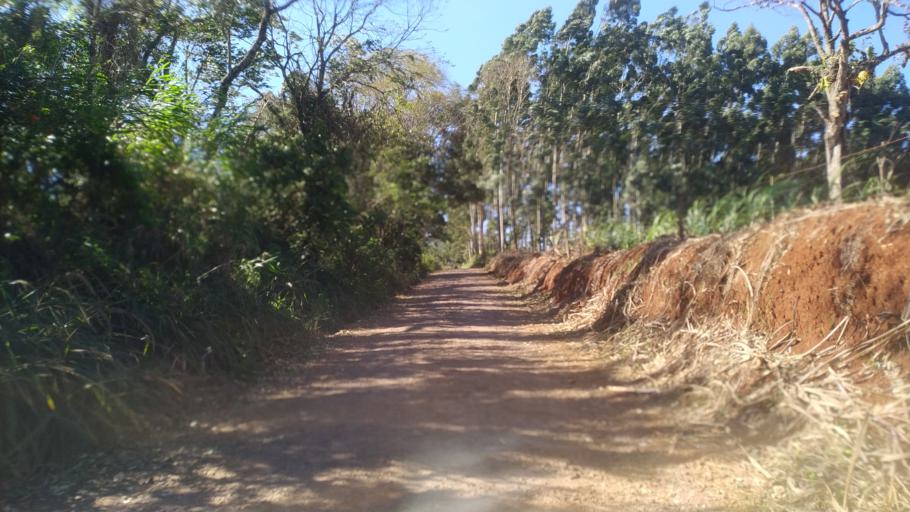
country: BR
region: Santa Catarina
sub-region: Chapeco
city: Chapeco
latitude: -27.1488
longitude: -52.6095
